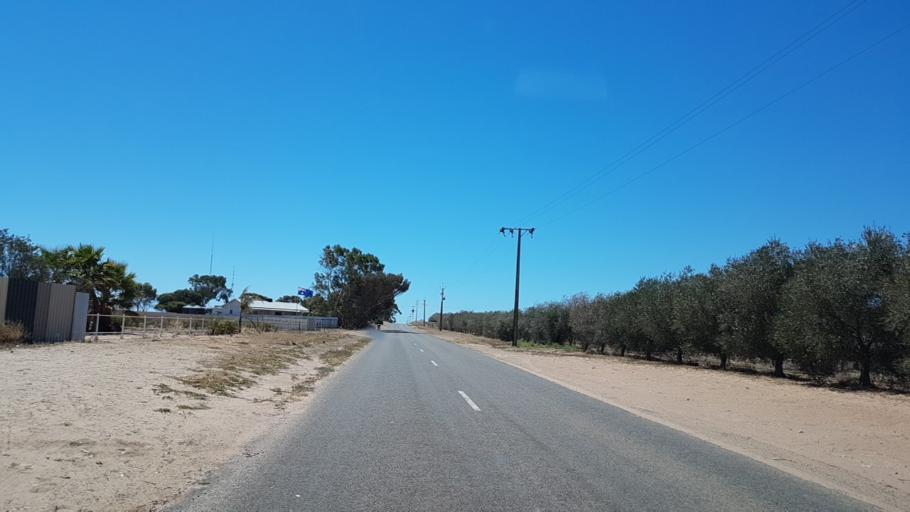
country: AU
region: South Australia
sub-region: Copper Coast
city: Wallaroo
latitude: -34.0509
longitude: 137.5930
